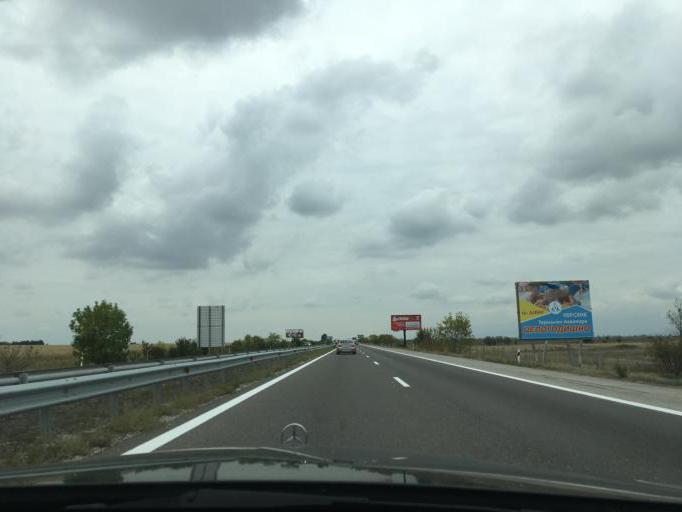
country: BG
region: Pazardzhik
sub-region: Obshtina Pazardzhik
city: Pazardzhik
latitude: 42.2560
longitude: 24.3302
